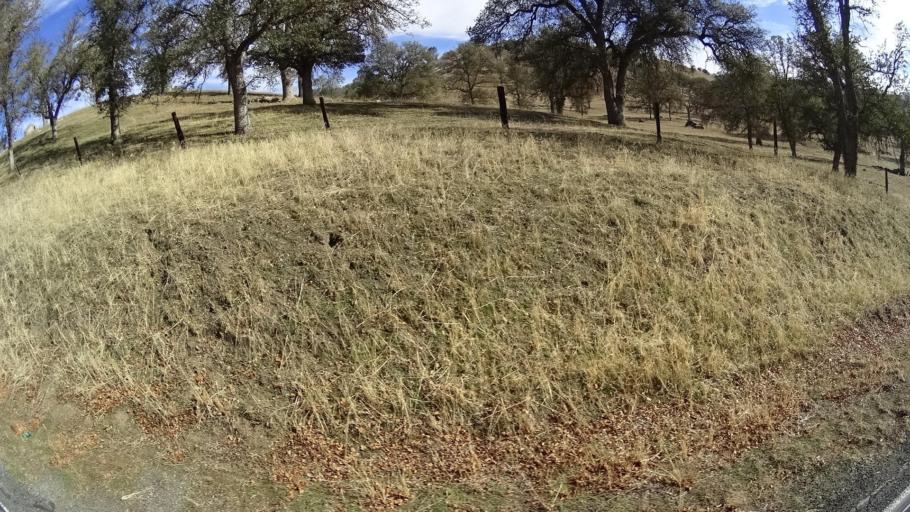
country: US
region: California
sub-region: Kern County
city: Alta Sierra
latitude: 35.6865
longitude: -118.7314
